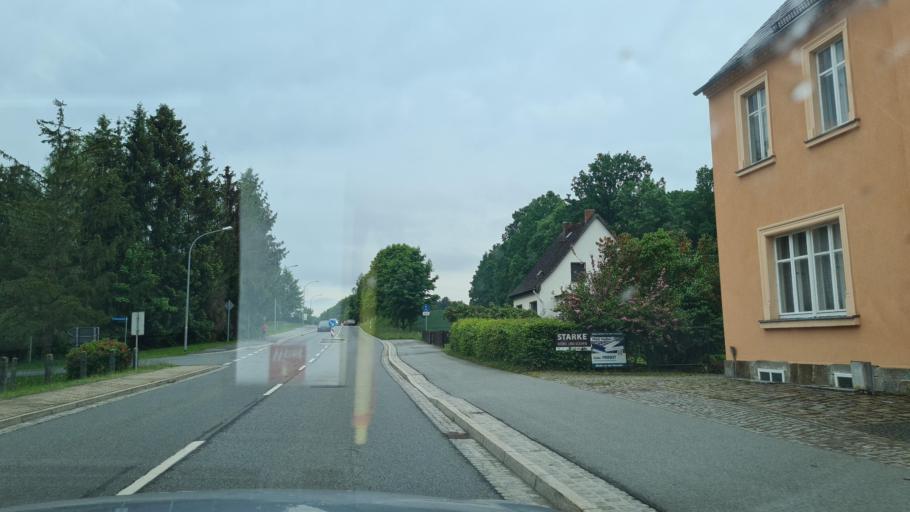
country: DE
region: Saxony
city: Schirgiswalde
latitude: 51.0651
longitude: 14.4295
